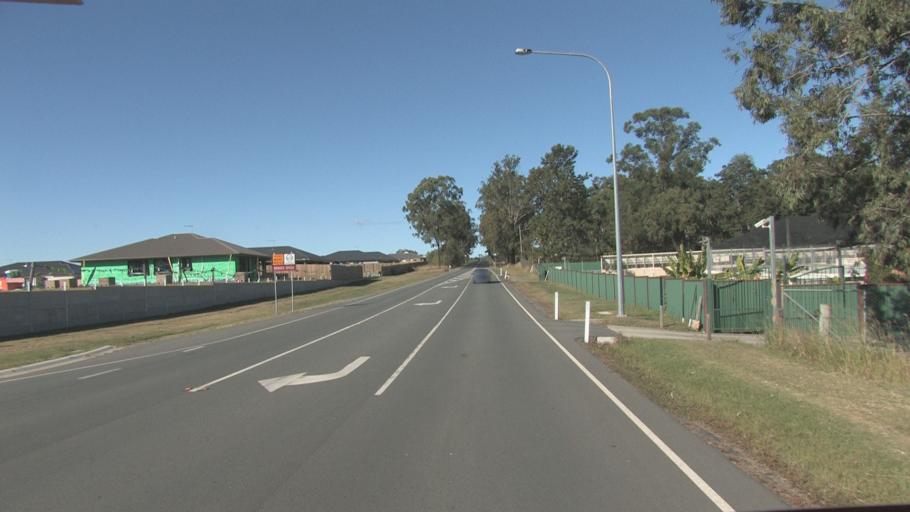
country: AU
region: Queensland
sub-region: Logan
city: Chambers Flat
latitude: -27.7781
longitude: 153.0965
